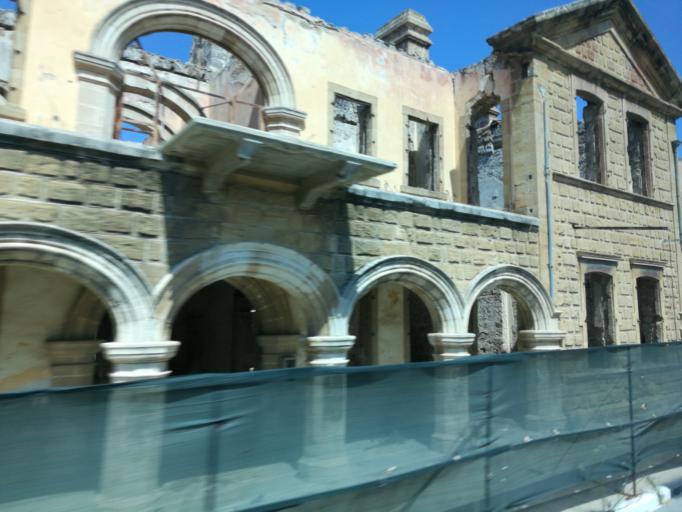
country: CY
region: Ammochostos
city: Famagusta
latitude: 35.1173
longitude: 33.9436
